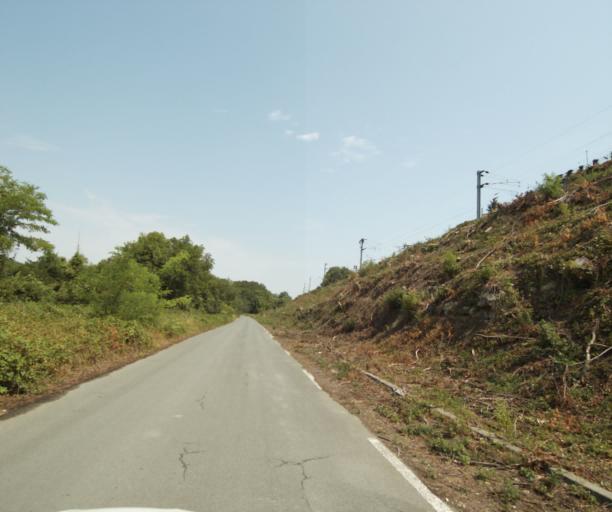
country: FR
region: Ile-de-France
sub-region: Departement des Yvelines
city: Maurecourt
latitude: 48.9991
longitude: 2.0729
